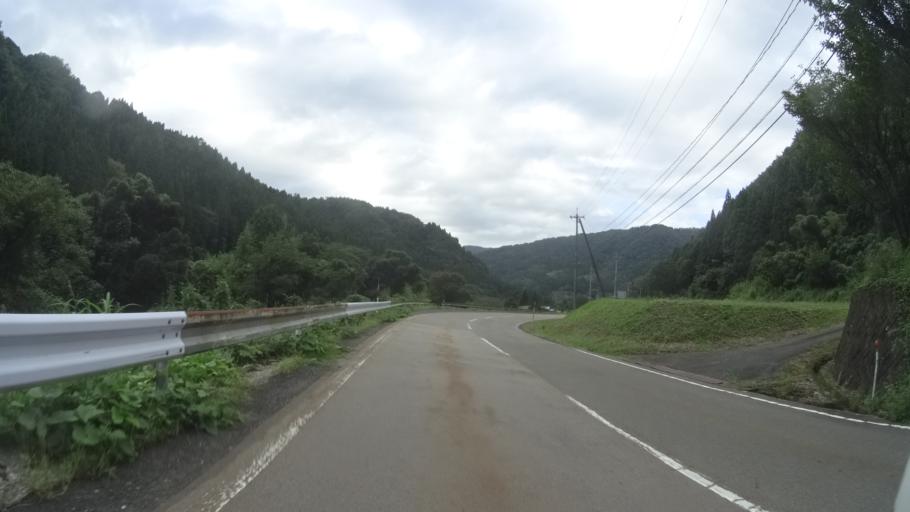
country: JP
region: Tottori
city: Kurayoshi
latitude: 35.4055
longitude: 133.9358
